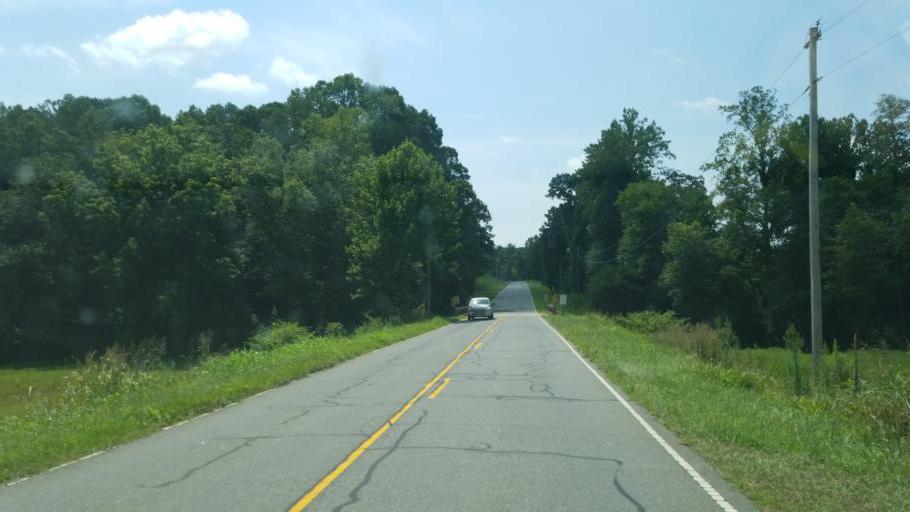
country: US
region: North Carolina
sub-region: Gaston County
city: Cherryville
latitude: 35.4187
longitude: -81.4102
